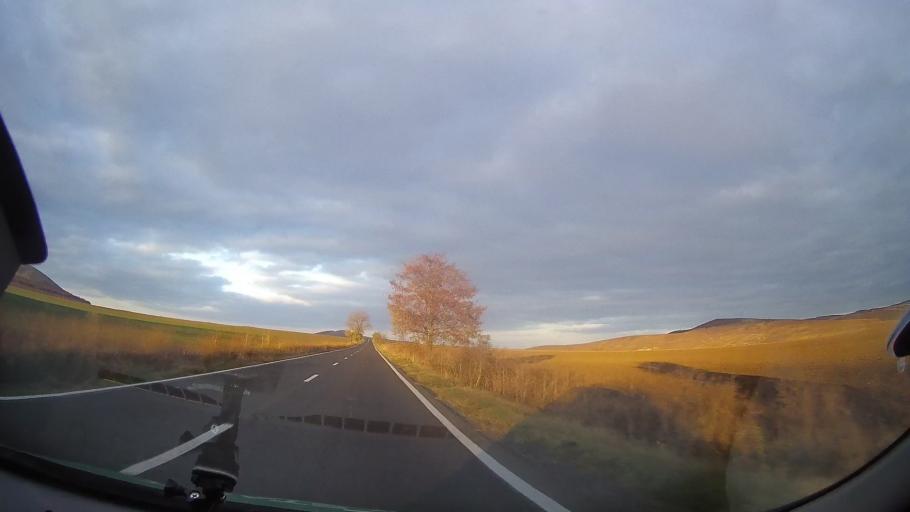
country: RO
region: Tulcea
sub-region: Comuna Nalbant
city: Nicolae Balcescu
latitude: 44.9755
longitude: 28.5442
